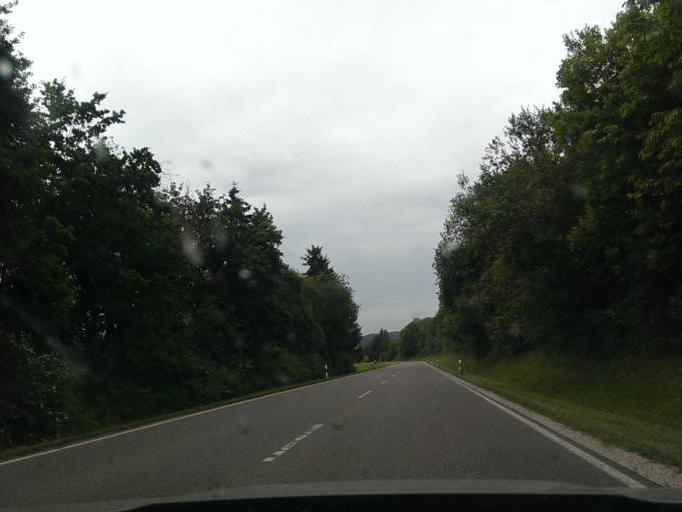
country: DE
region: Bavaria
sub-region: Upper Palatinate
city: Berching
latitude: 49.0234
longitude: 11.4493
